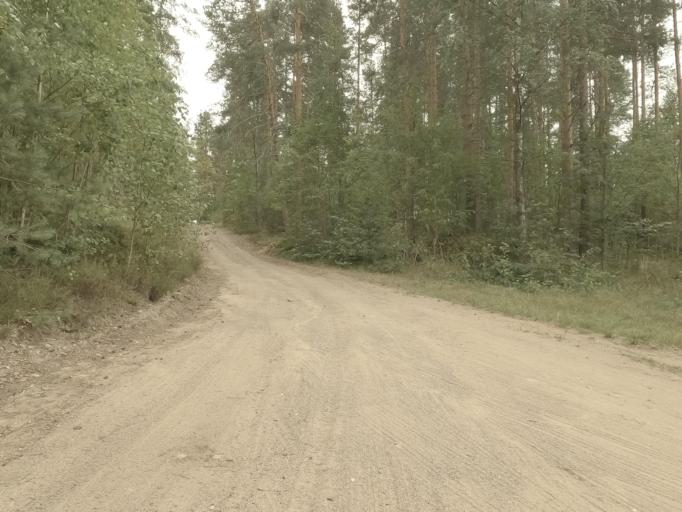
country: RU
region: Leningrad
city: Kamennogorsk
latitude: 60.9967
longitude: 29.1830
